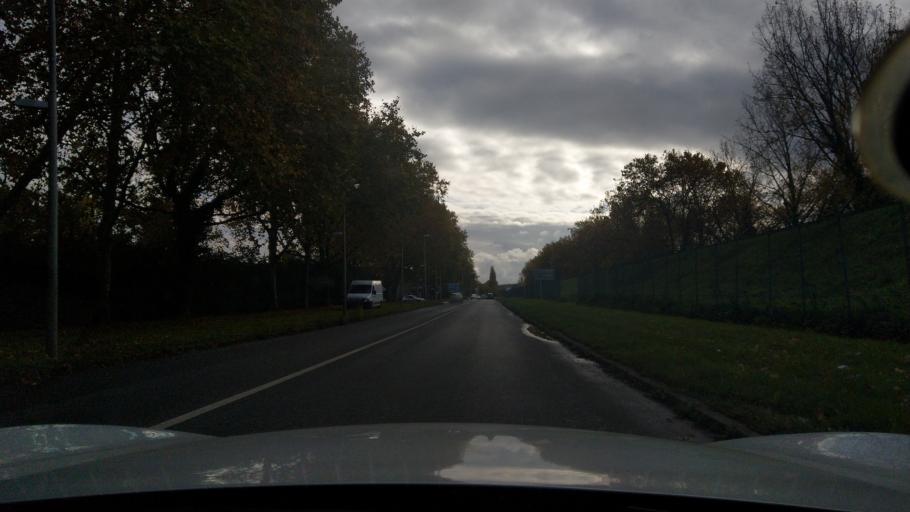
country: FR
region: Ile-de-France
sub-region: Departement de l'Essonne
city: Grigny
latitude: 48.6334
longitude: 2.3956
